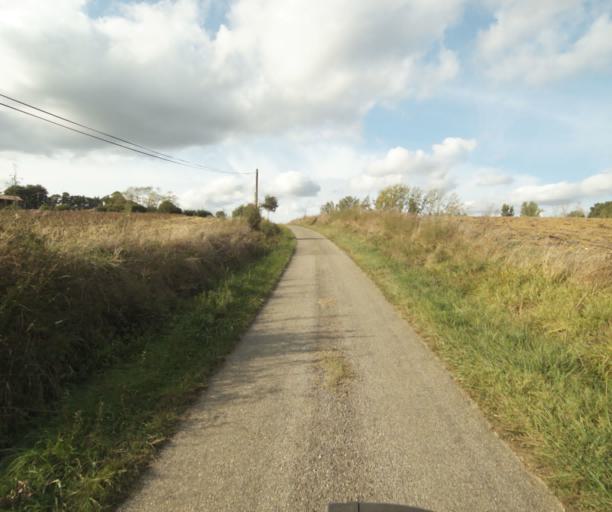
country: FR
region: Midi-Pyrenees
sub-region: Departement du Tarn-et-Garonne
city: Verdun-sur-Garonne
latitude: 43.8384
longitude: 1.1481
